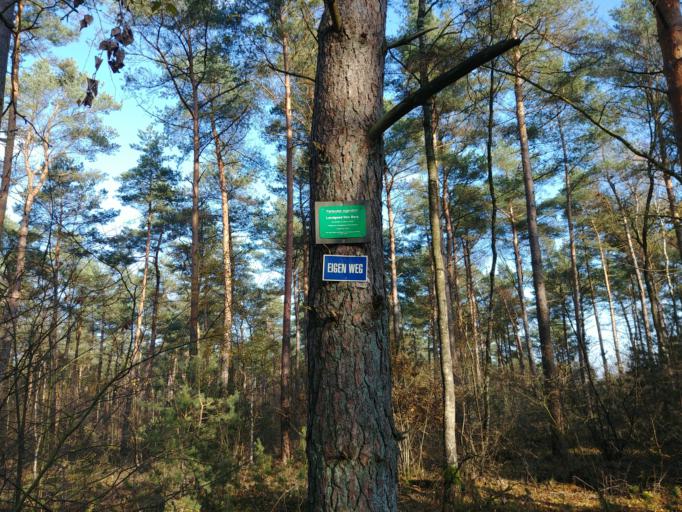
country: NL
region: Utrecht
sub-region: Gemeente Utrechtse Heuvelrug
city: Leersum
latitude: 52.0256
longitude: 5.4367
